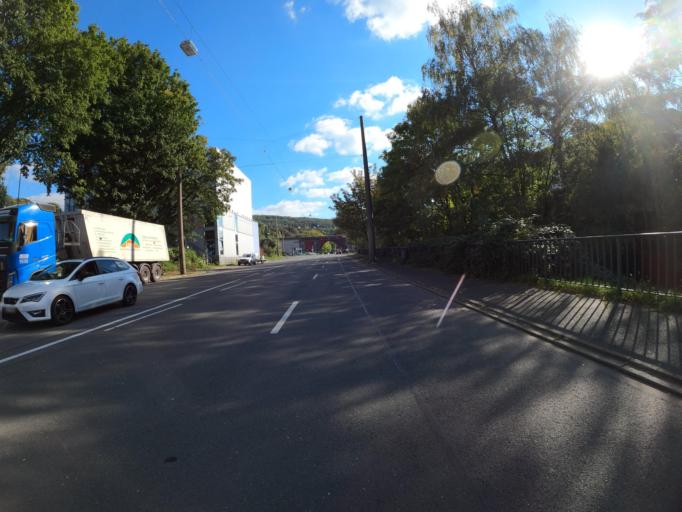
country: DE
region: North Rhine-Westphalia
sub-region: Regierungsbezirk Arnsberg
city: Schwelm
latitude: 51.2690
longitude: 7.2349
